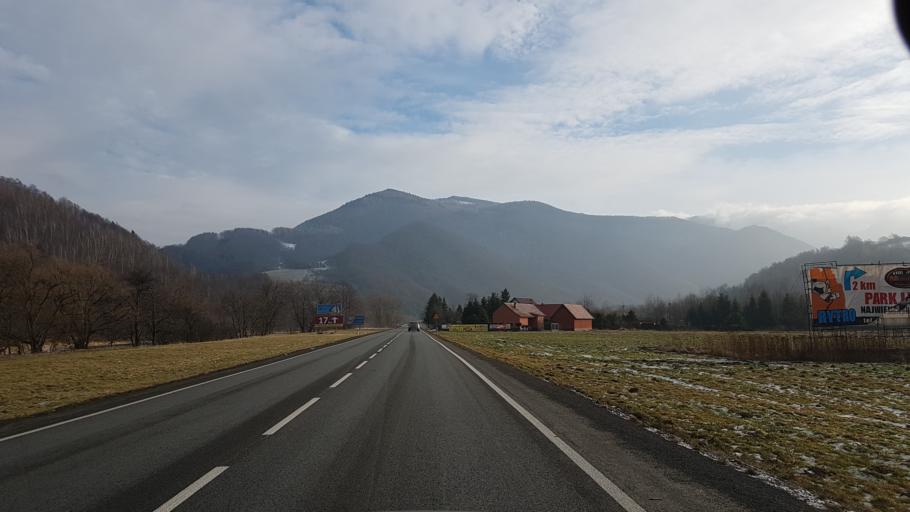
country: PL
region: Lesser Poland Voivodeship
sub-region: Powiat nowosadecki
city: Rytro
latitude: 49.5000
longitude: 20.6665
